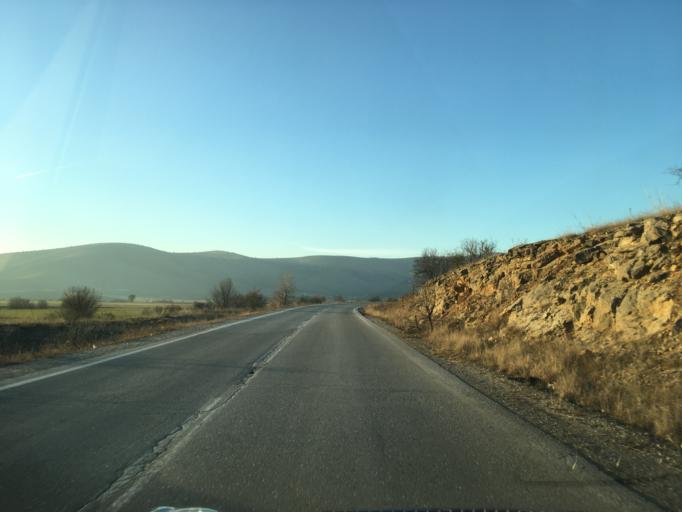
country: GR
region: West Macedonia
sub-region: Nomos Kozanis
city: Kozani
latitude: 40.3095
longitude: 21.7331
